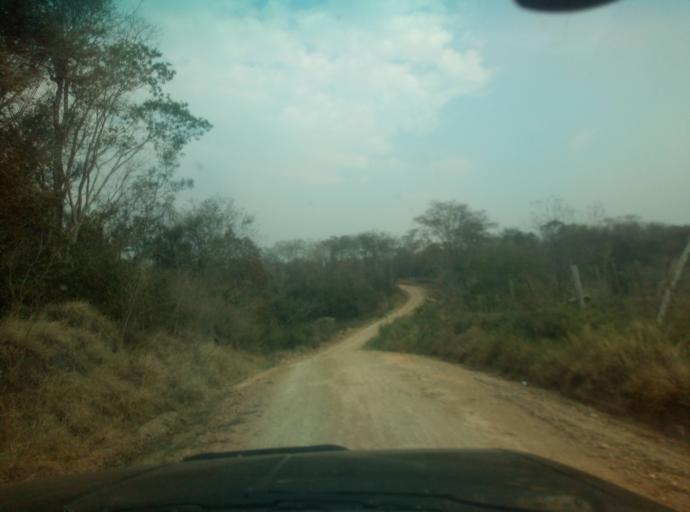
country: PY
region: Caaguazu
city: San Joaquin
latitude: -25.0920
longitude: -56.1412
